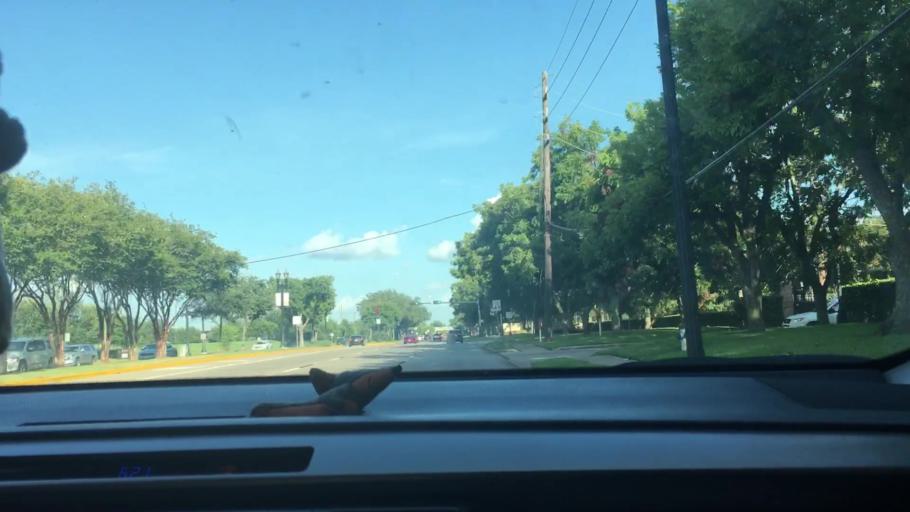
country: US
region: Texas
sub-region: Fort Bend County
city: Sugar Land
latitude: 29.6010
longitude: -95.6300
